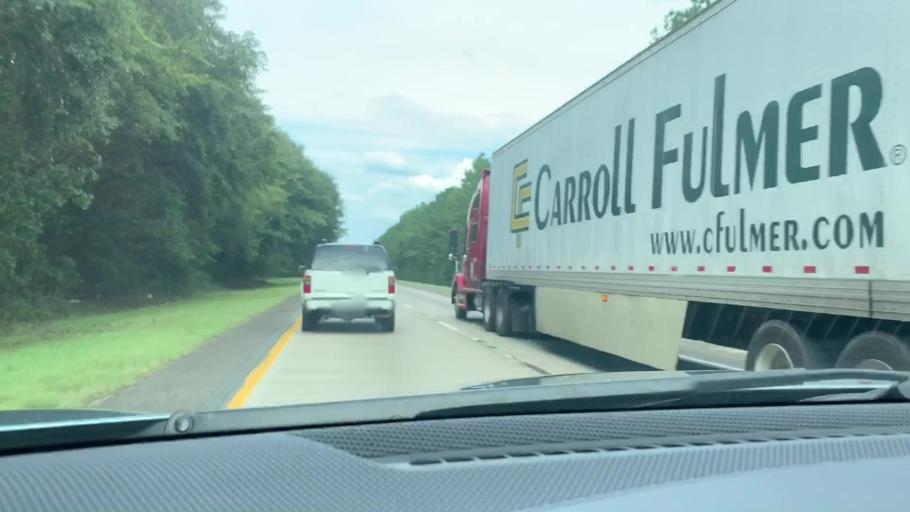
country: US
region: South Carolina
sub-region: Hampton County
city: Yemassee
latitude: 32.7679
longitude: -80.8072
